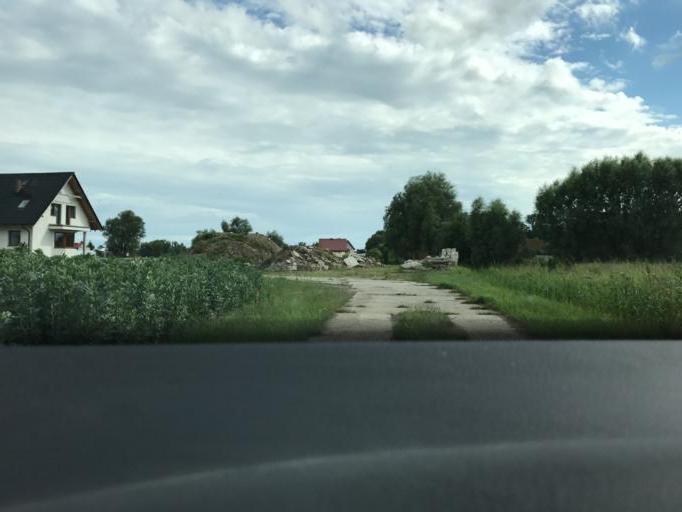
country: PL
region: Pomeranian Voivodeship
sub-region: Powiat gdanski
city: Pruszcz Gdanski
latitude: 54.2970
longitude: 18.7231
